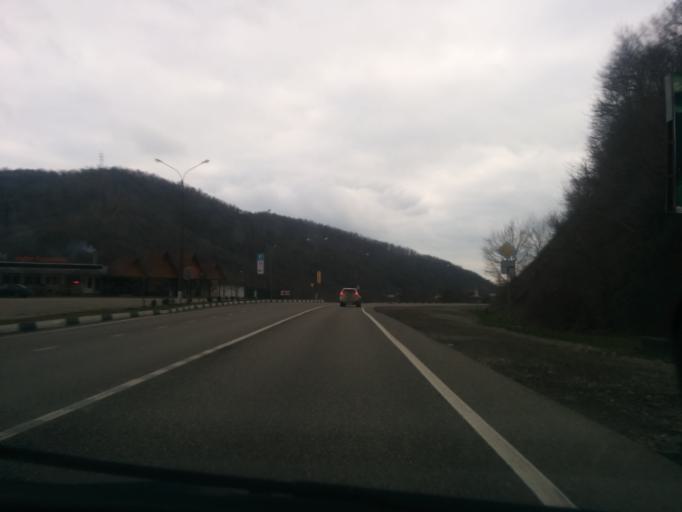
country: RU
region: Krasnodarskiy
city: Ol'ginka
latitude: 44.2145
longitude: 38.8947
